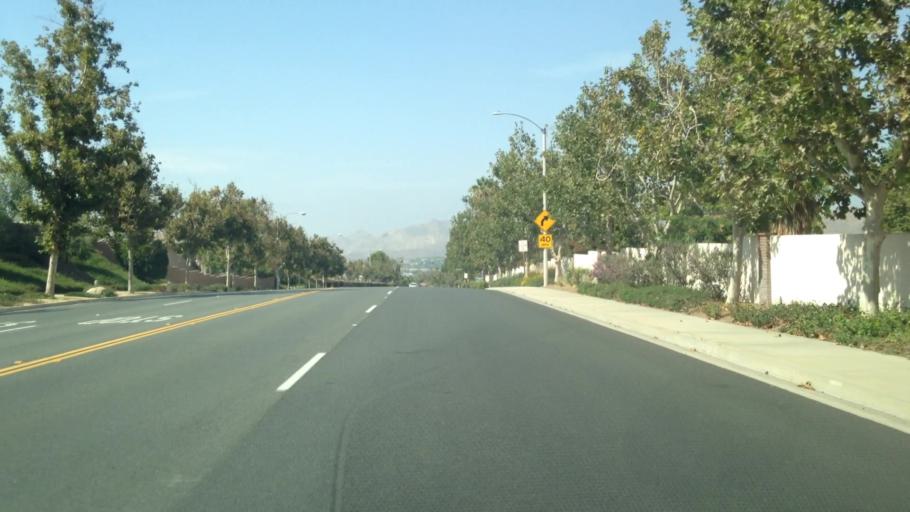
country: US
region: California
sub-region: Riverside County
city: El Cerrito
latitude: 33.7835
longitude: -117.5026
